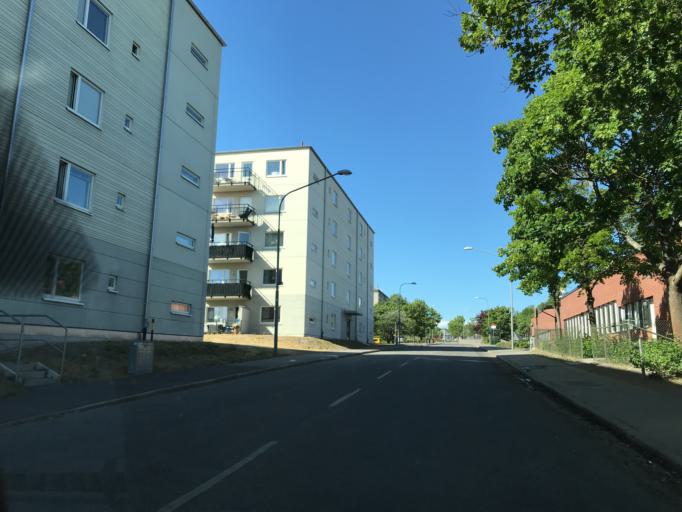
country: SE
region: Stockholm
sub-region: Huddinge Kommun
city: Segeltorp
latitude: 59.2901
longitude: 17.9391
